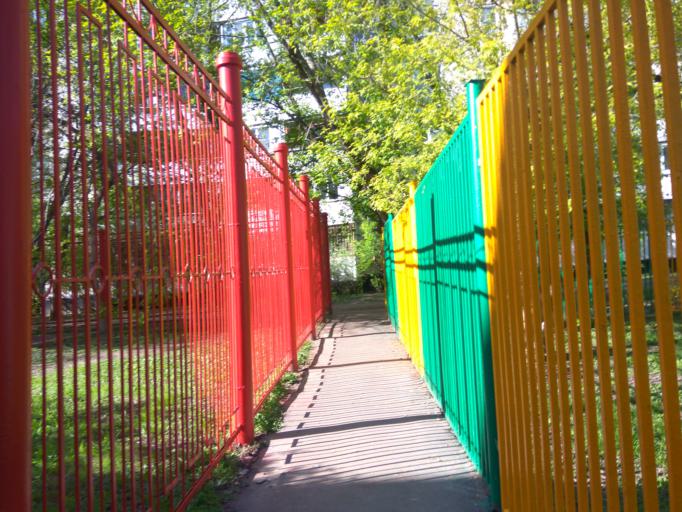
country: RU
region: Moscow
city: Kolomenskoye
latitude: 55.6783
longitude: 37.6730
